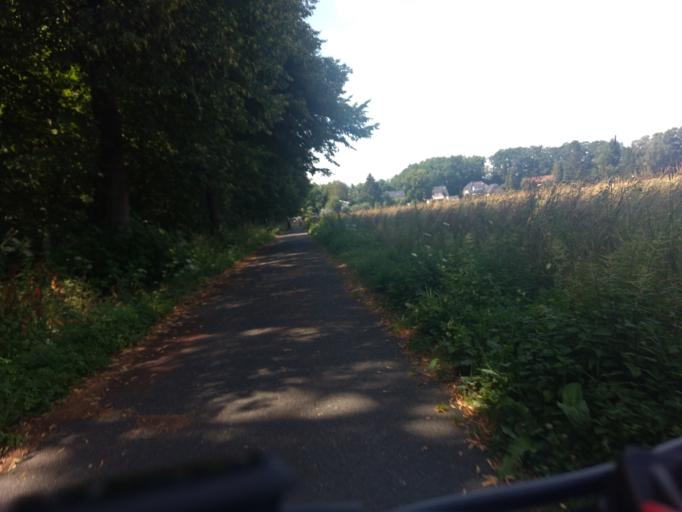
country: DE
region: North Rhine-Westphalia
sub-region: Regierungsbezirk Detmold
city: Hovelhof
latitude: 51.7628
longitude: 8.6714
